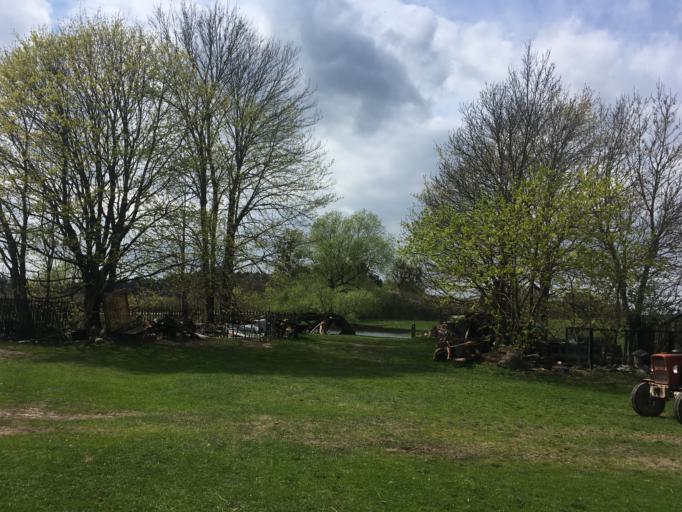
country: PL
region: Warmian-Masurian Voivodeship
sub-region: Powiat goldapski
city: Banie Mazurskie
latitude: 54.2105
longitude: 22.1828
